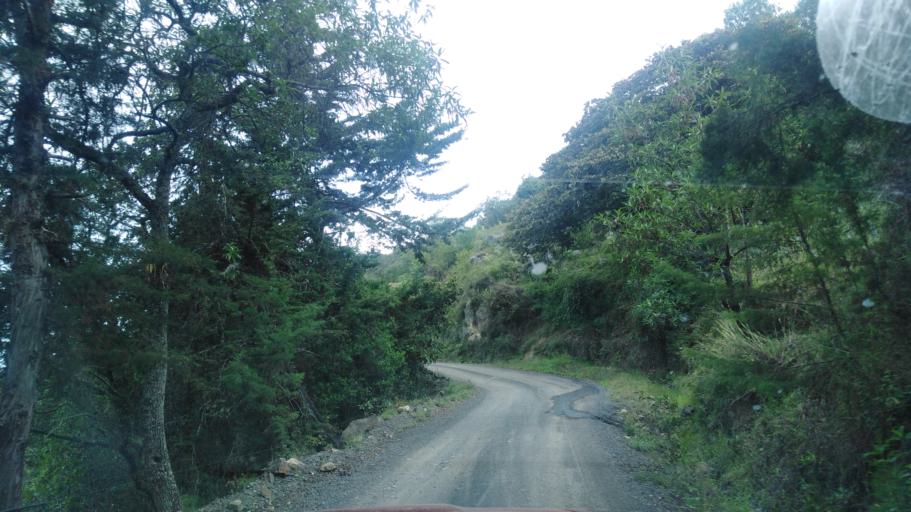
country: CO
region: Boyaca
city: San Mateo
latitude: 6.4451
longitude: -72.5754
